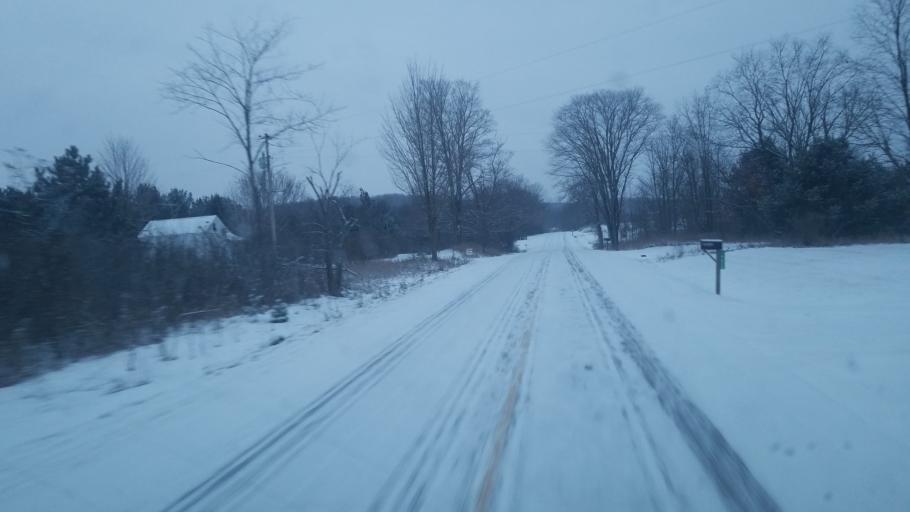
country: US
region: Michigan
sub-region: Osceola County
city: Reed City
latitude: 43.8218
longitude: -85.4166
